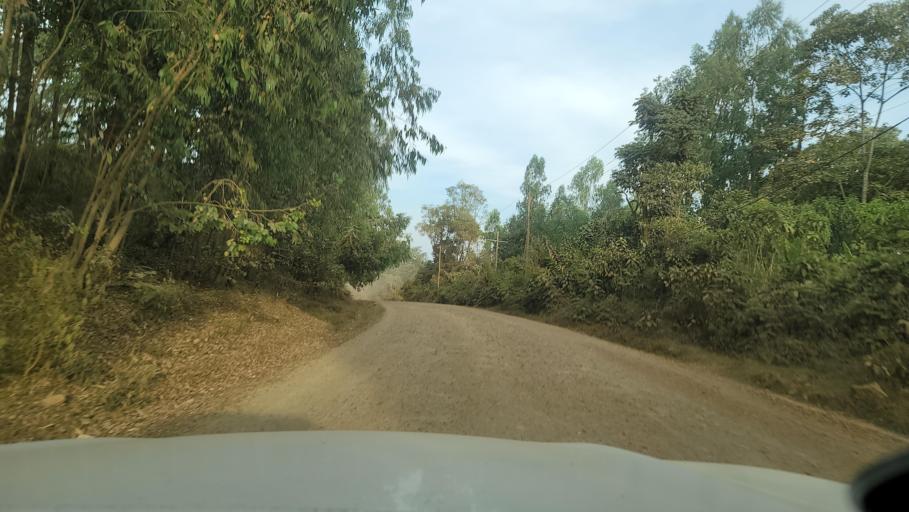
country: ET
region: Oromiya
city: Agaro
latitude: 7.8396
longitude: 36.5463
